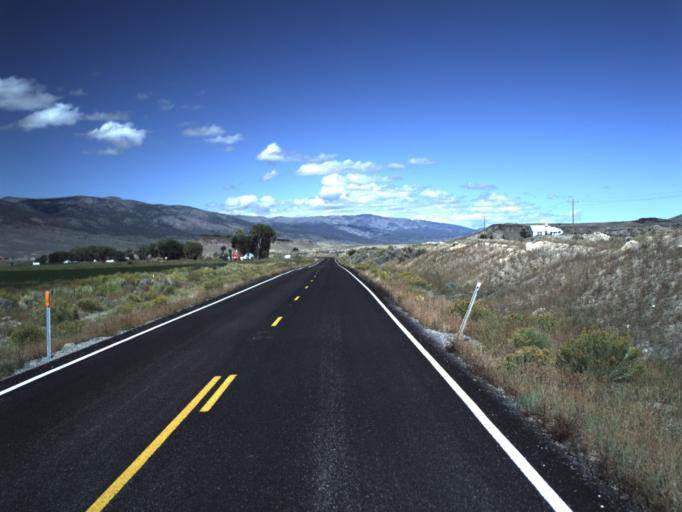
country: US
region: Utah
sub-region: Piute County
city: Junction
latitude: 38.1402
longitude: -111.9978
